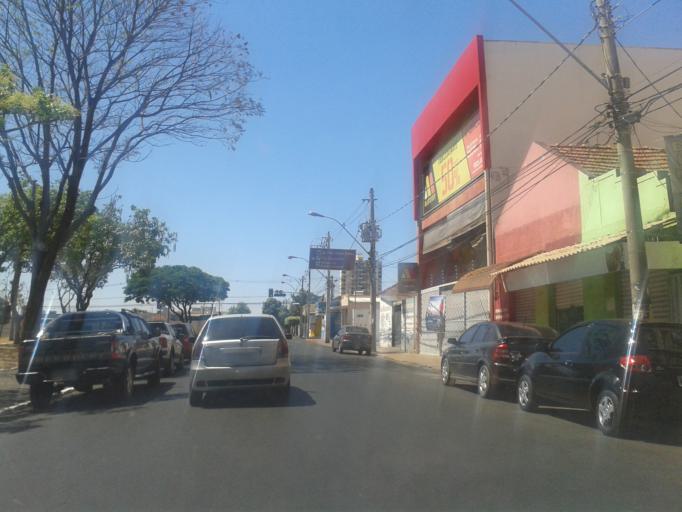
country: BR
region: Minas Gerais
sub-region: Uberlandia
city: Uberlandia
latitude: -18.9110
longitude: -48.2752
